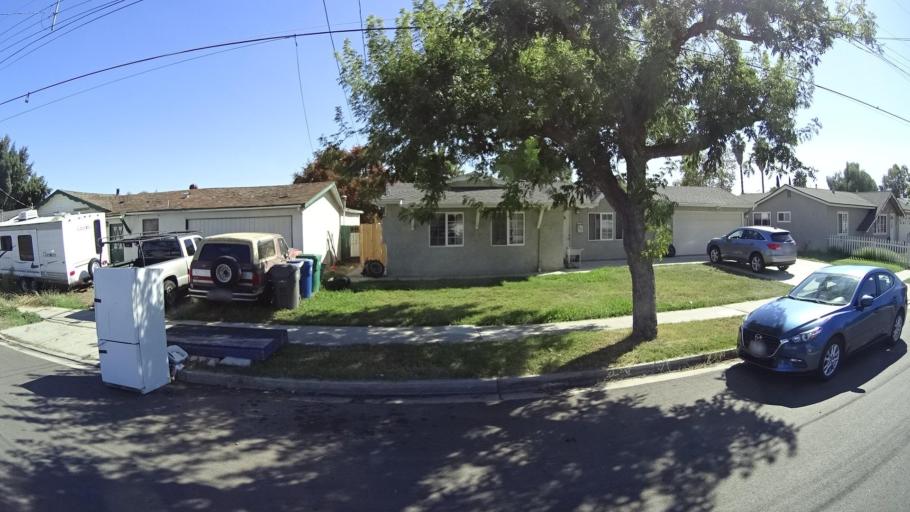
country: US
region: California
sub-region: San Diego County
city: La Presa
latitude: 32.7077
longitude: -117.0152
